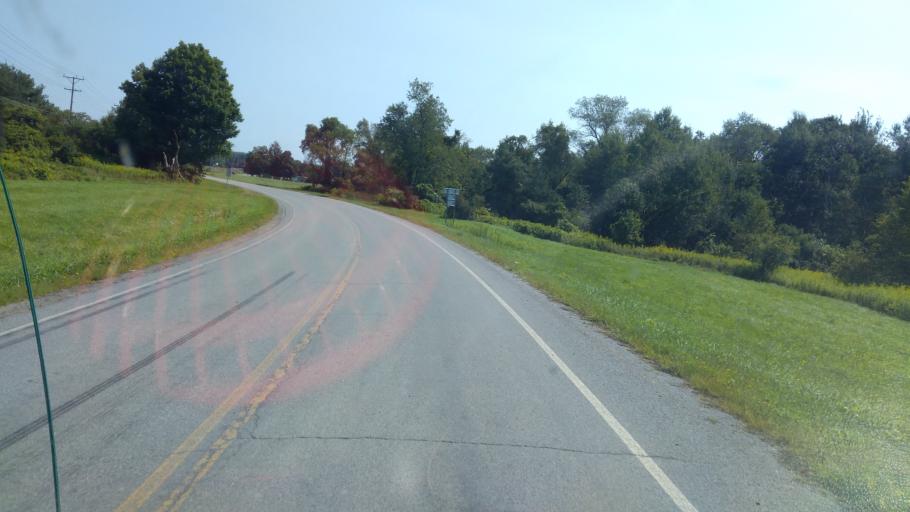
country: US
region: New York
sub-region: Allegany County
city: Friendship
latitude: 42.2151
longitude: -78.1121
